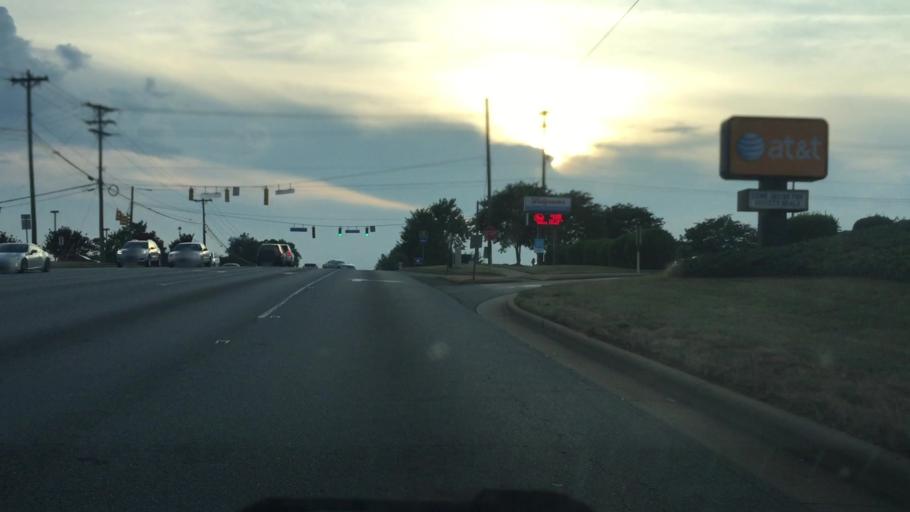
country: US
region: North Carolina
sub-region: Iredell County
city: Mooresville
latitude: 35.5950
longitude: -80.8677
